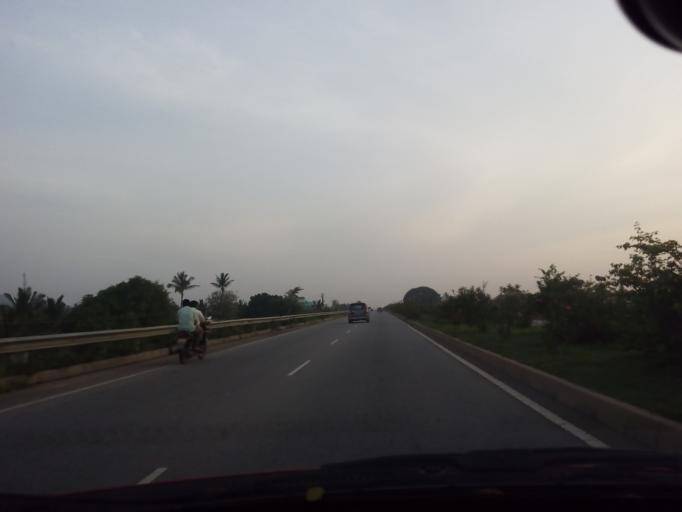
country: IN
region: Karnataka
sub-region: Bangalore Rural
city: Devanhalli
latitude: 13.3236
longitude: 77.7255
